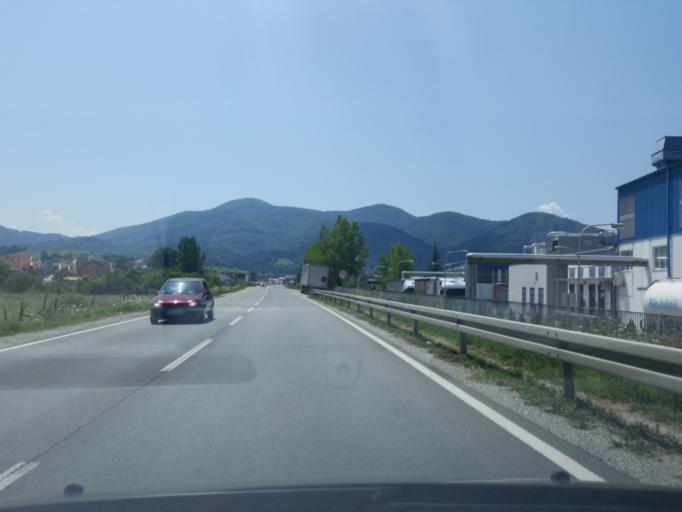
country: RS
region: Central Serbia
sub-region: Moravicki Okrug
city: Gornji Milanovac
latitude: 44.0163
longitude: 20.4635
